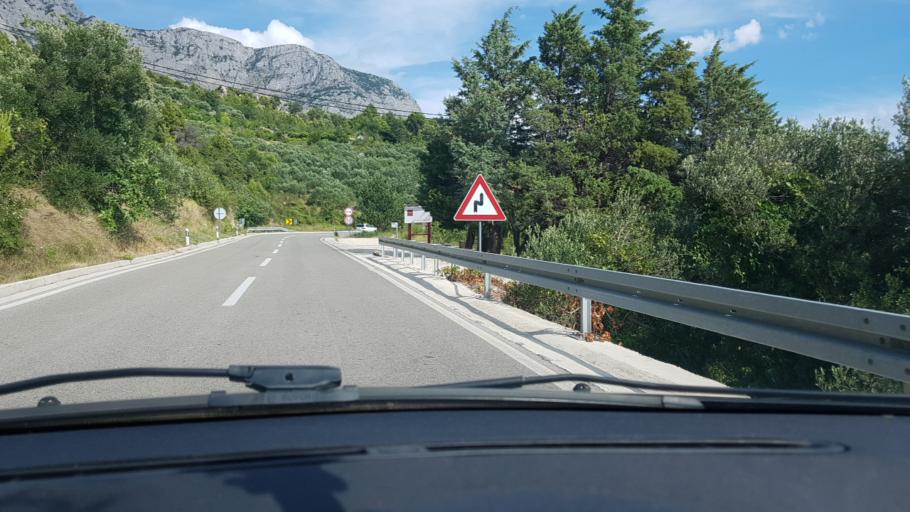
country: HR
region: Splitsko-Dalmatinska
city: Tucepi
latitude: 43.2779
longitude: 17.0617
